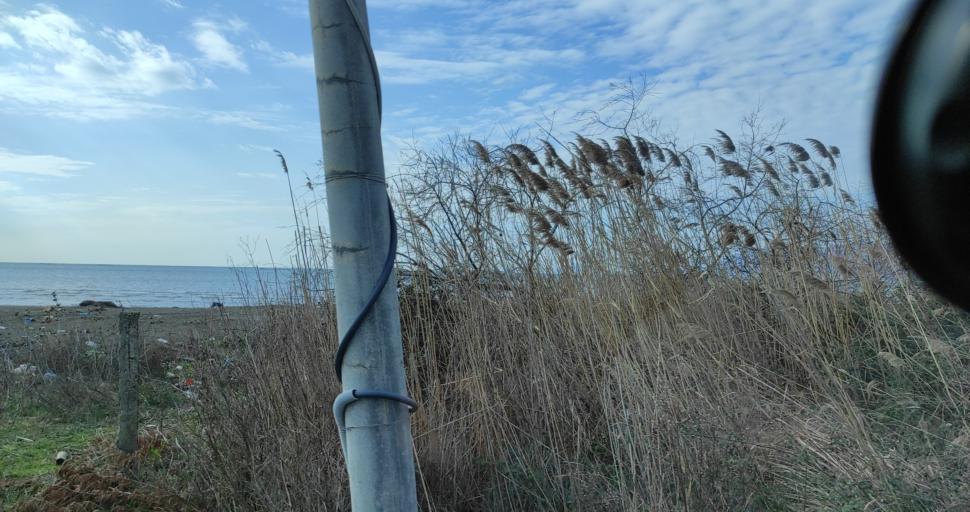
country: AL
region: Lezhe
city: Shengjin
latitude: 41.7716
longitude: 19.6013
